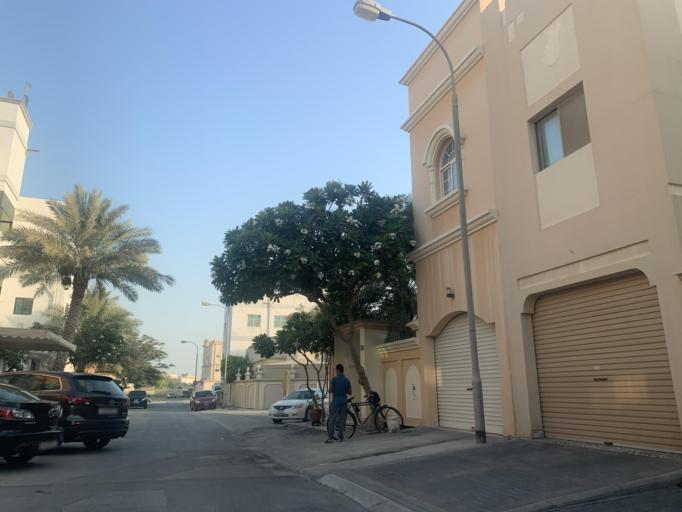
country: BH
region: Manama
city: Jidd Hafs
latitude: 26.2141
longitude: 50.5313
